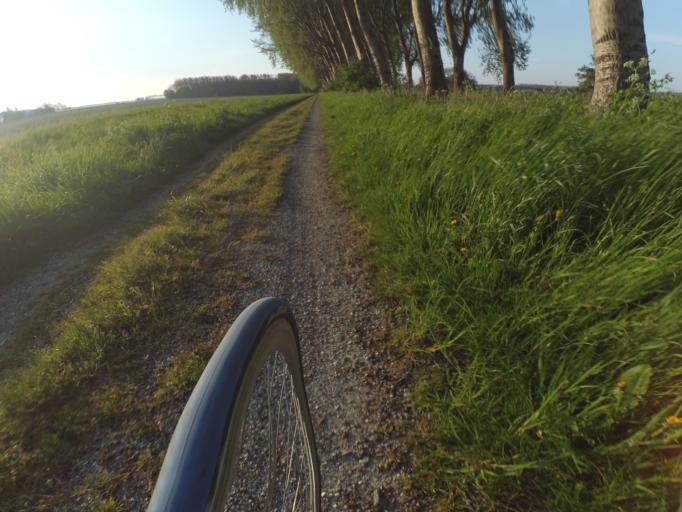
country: NL
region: Flevoland
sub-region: Gemeente Lelystad
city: Lelystad
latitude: 52.4368
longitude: 5.4859
